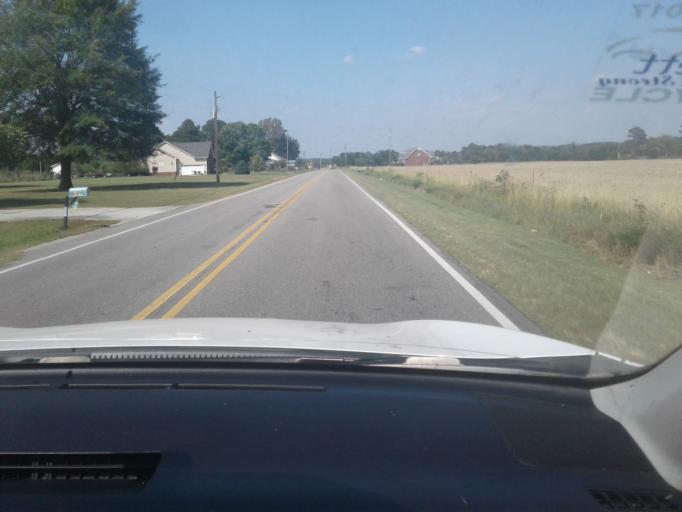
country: US
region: North Carolina
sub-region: Harnett County
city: Coats
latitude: 35.3732
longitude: -78.6280
